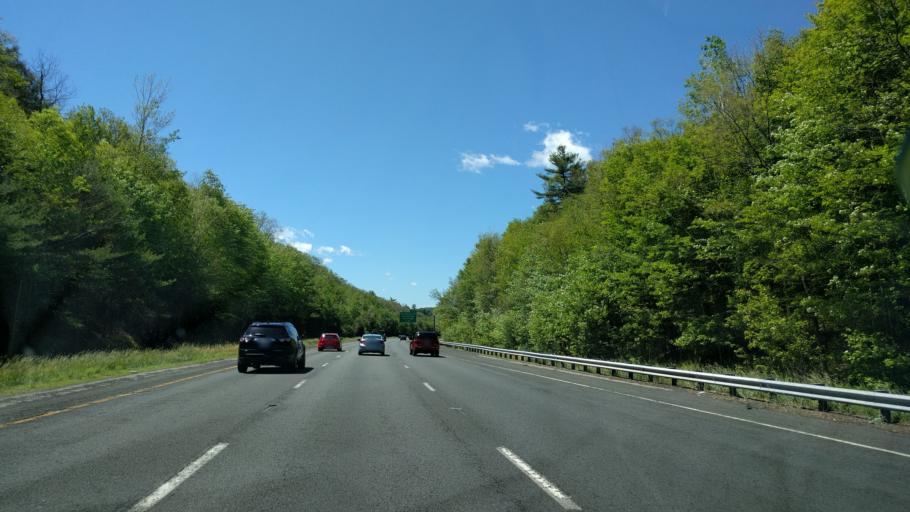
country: US
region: Massachusetts
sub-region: Worcester County
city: Sturbridge
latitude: 42.0794
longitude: -72.0991
